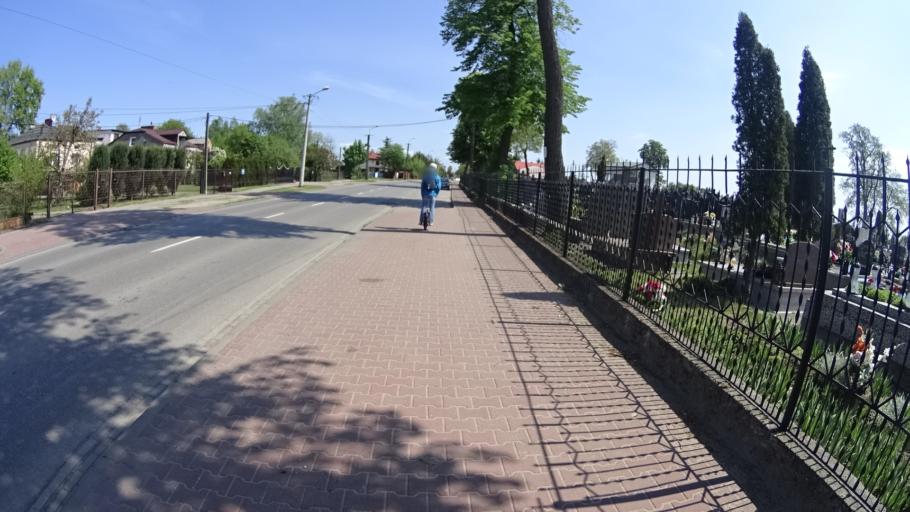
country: PL
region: Masovian Voivodeship
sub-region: Powiat warszawski zachodni
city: Jozefow
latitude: 52.2539
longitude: 20.7277
